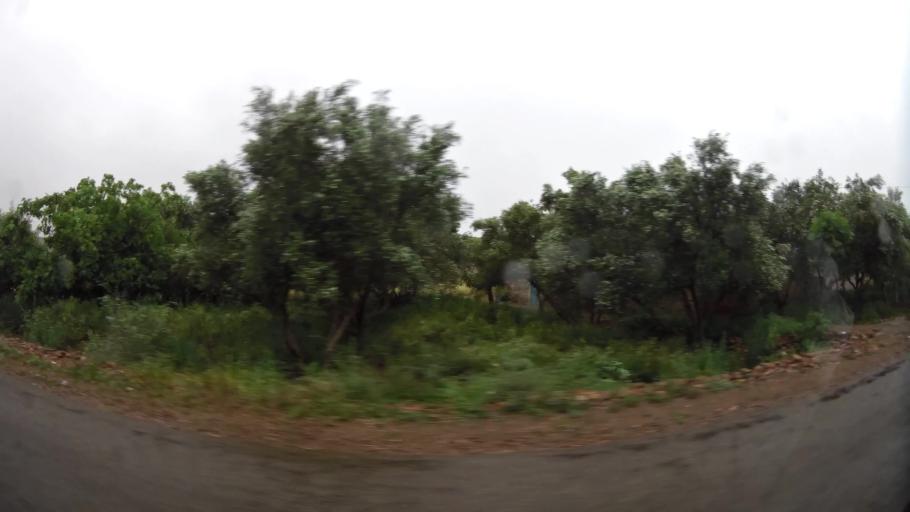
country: MA
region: Oriental
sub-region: Nador
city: Boudinar
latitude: 35.1199
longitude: -3.5747
